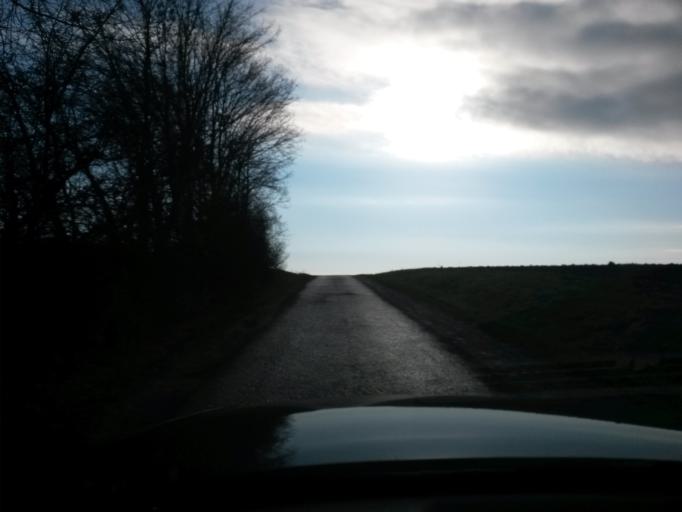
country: DE
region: Bavaria
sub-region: Regierungsbezirk Unterfranken
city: Rimpar
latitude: 49.8395
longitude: 9.9434
